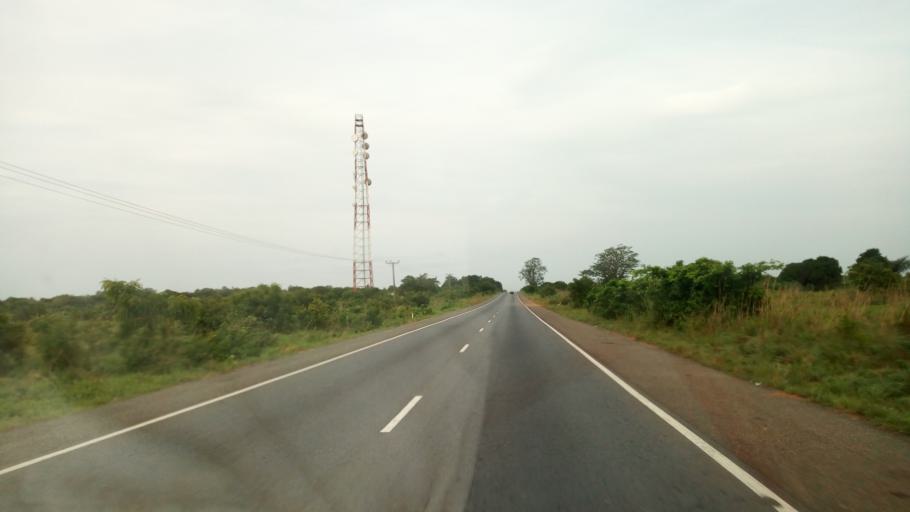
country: GH
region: Volta
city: Keta
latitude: 6.0631
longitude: 1.0046
